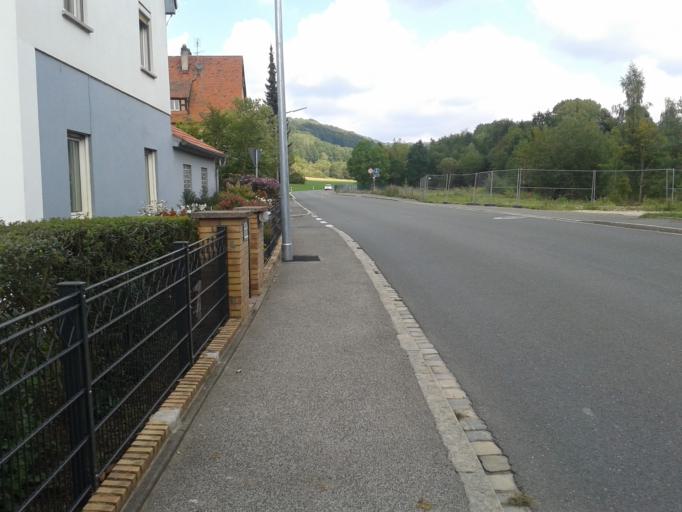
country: DE
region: Bavaria
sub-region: Regierungsbezirk Mittelfranken
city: Simmelsdorf
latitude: 49.5994
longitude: 11.3423
